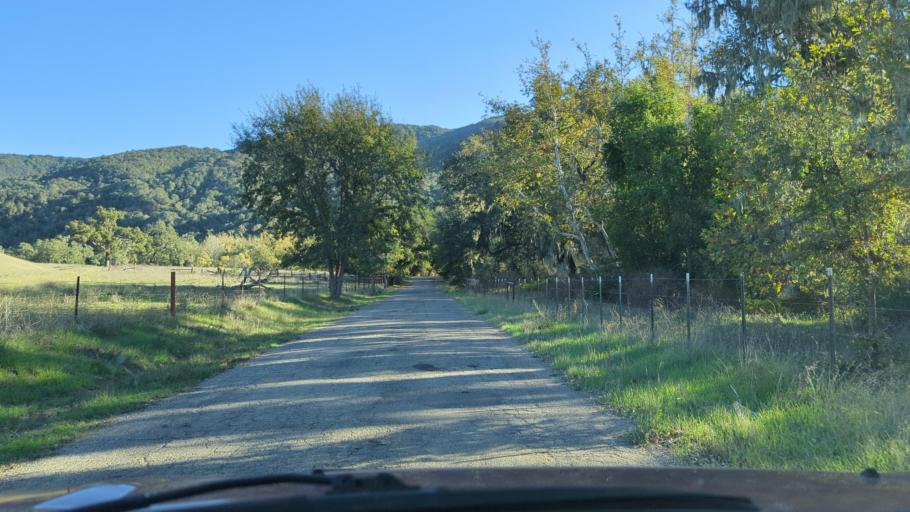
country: US
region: California
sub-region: Santa Barbara County
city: Santa Ynez
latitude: 34.5572
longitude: -120.0831
